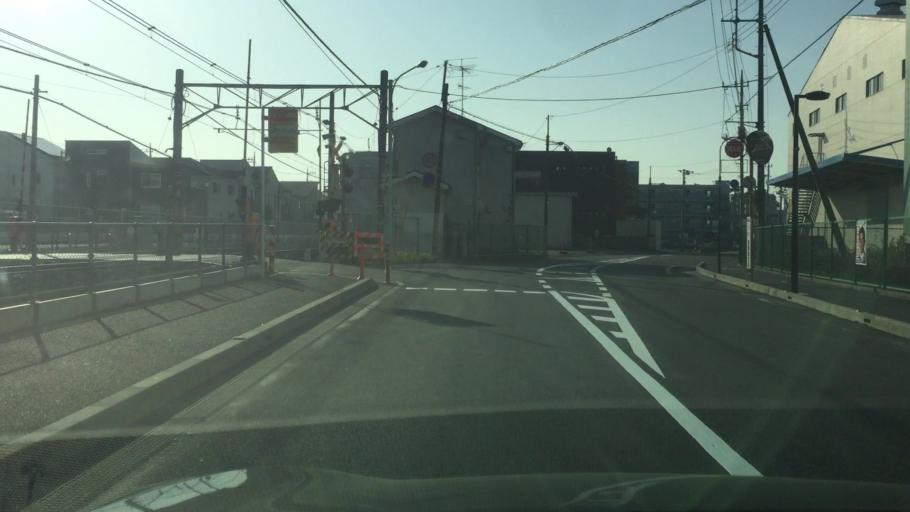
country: JP
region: Saitama
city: Ageoshimo
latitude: 35.9336
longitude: 139.6124
